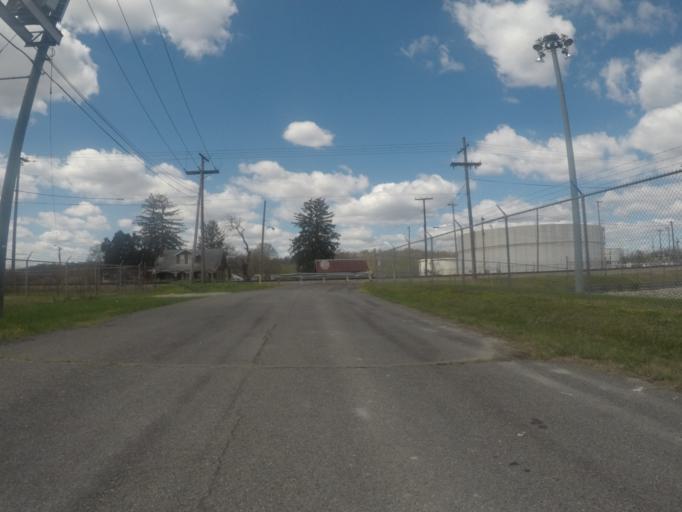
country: US
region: Kentucky
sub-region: Boyd County
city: Catlettsburg
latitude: 38.4049
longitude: -82.5898
